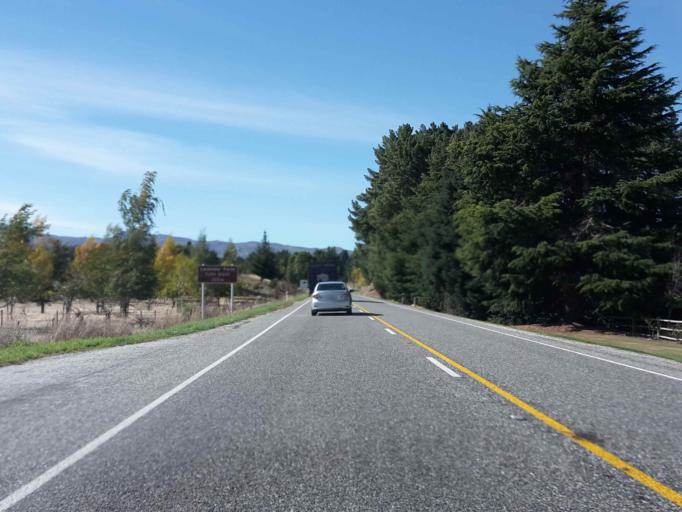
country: NZ
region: Otago
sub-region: Queenstown-Lakes District
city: Wanaka
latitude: -44.7007
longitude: 169.1833
